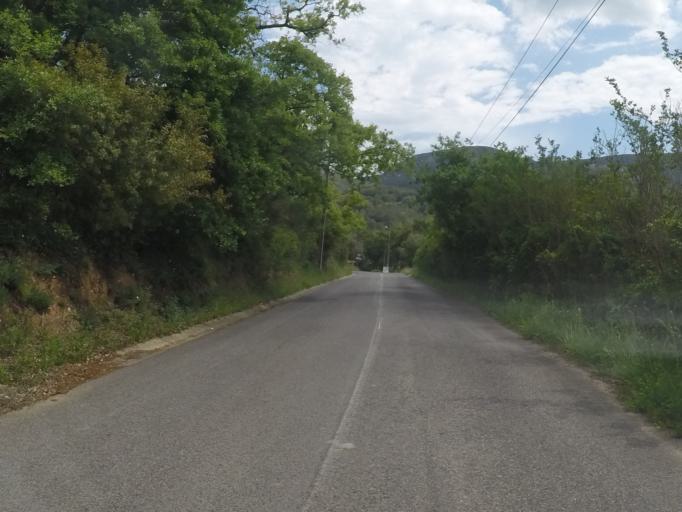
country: PT
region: Setubal
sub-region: Palmela
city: Quinta do Anjo
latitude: 38.5008
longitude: -8.9982
